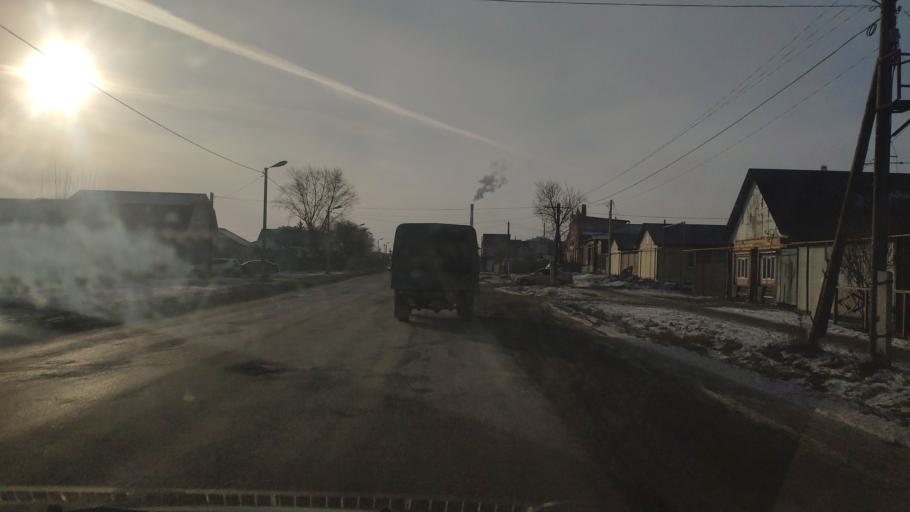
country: RU
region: Kurgan
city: Shadrinsk
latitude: 56.0891
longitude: 63.6752
